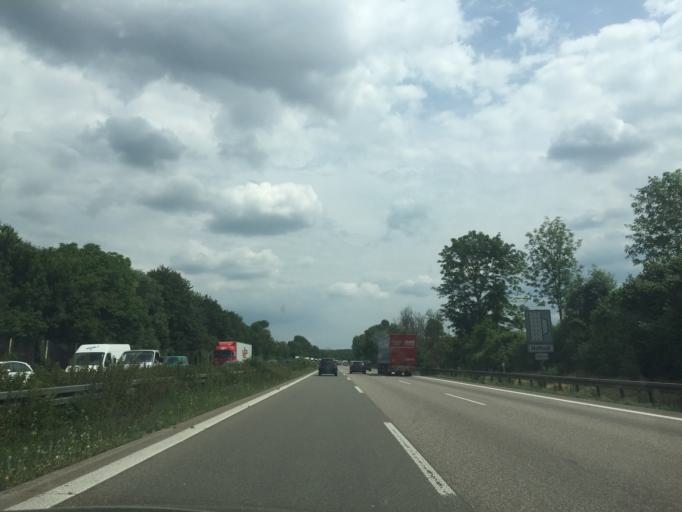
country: DE
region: Baden-Wuerttemberg
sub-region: Karlsruhe Region
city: Balzfeld
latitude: 49.2671
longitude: 8.7873
